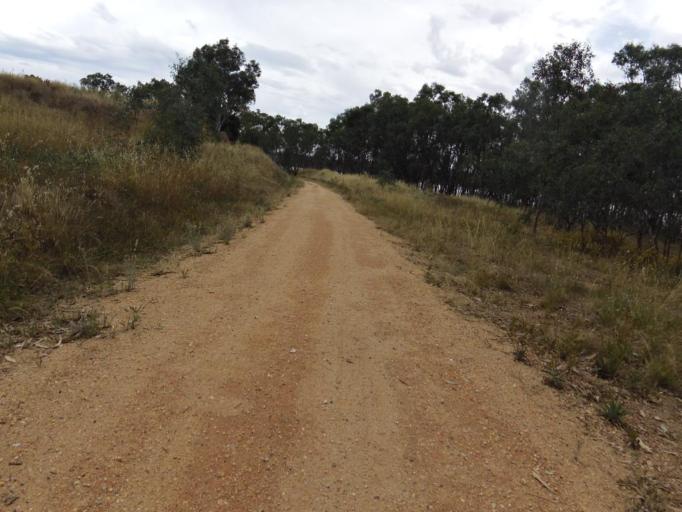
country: AU
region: Victoria
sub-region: Greater Bendigo
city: Kennington
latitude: -36.8667
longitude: 144.6232
